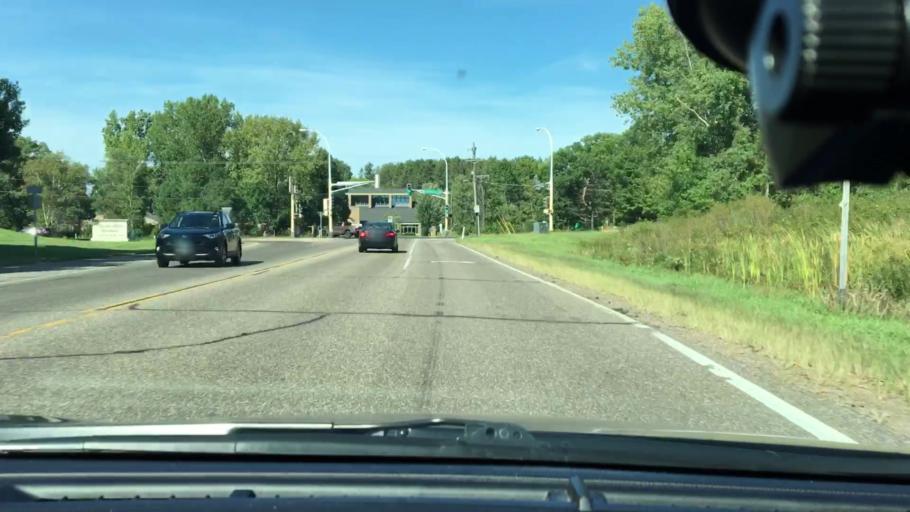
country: US
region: Minnesota
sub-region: Washington County
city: Mahtomedi
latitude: 45.0563
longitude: -92.9474
